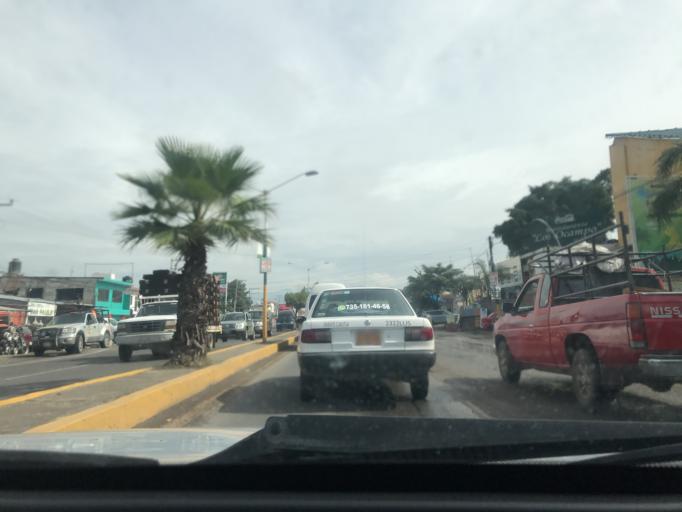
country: MX
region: Morelos
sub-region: Cuautla
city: Tierra Larga (Campo Nuevo)
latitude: 18.8542
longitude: -98.9364
